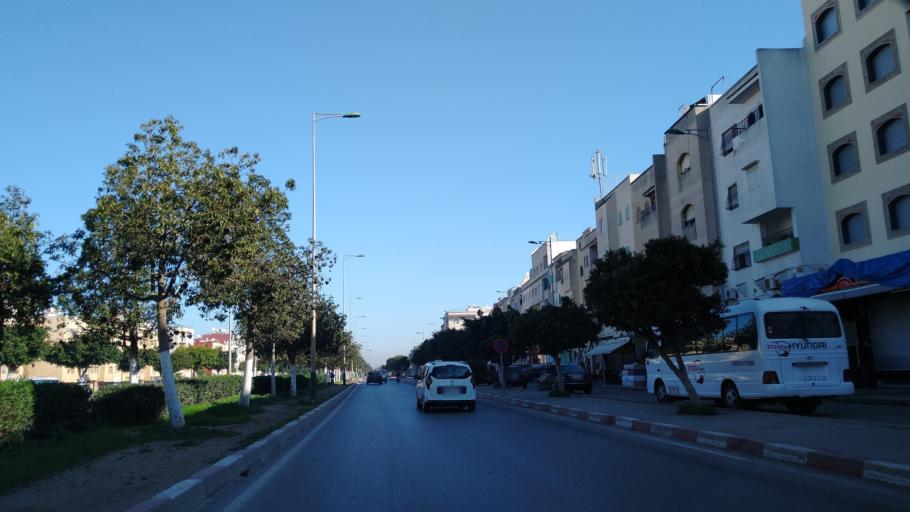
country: MA
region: Rabat-Sale-Zemmour-Zaer
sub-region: Skhirate-Temara
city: Temara
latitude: 33.9273
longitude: -6.8930
